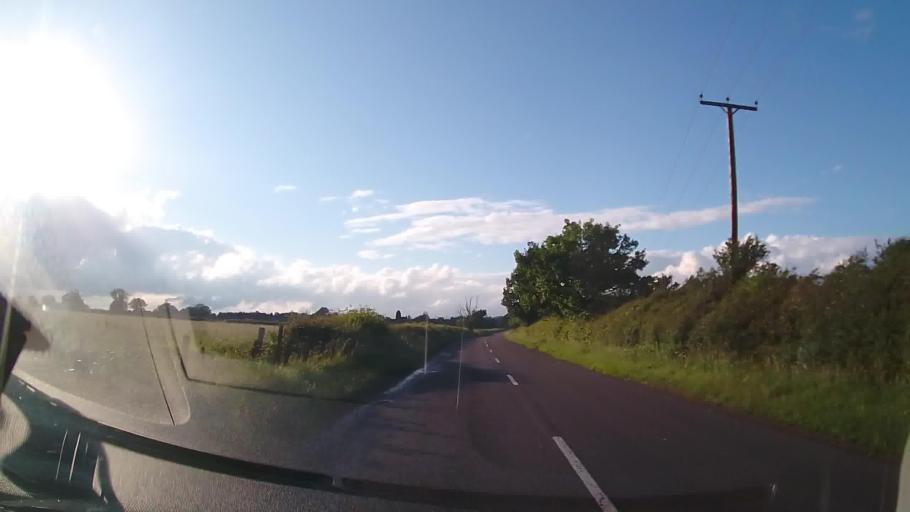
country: GB
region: England
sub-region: Leicestershire
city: Markfield
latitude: 52.6706
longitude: -1.2720
